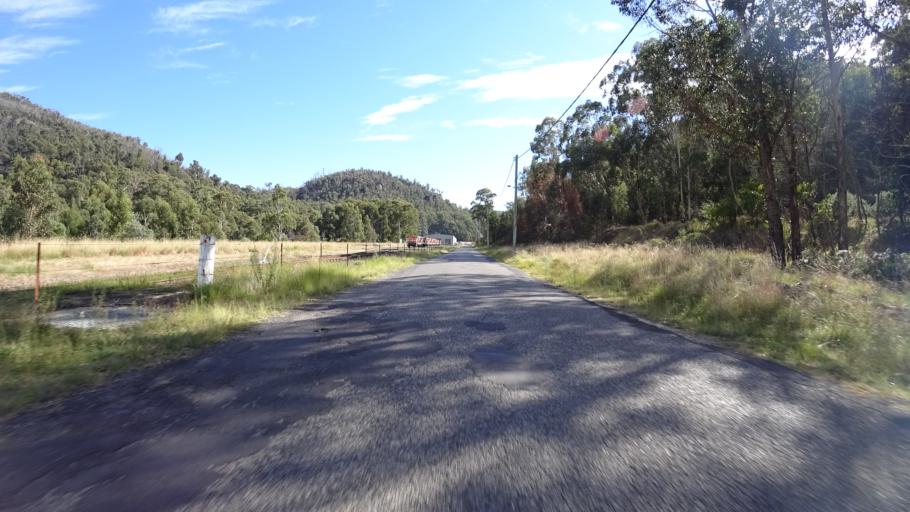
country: AU
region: New South Wales
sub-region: Lithgow
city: Lithgow
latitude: -33.4639
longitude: 150.1689
